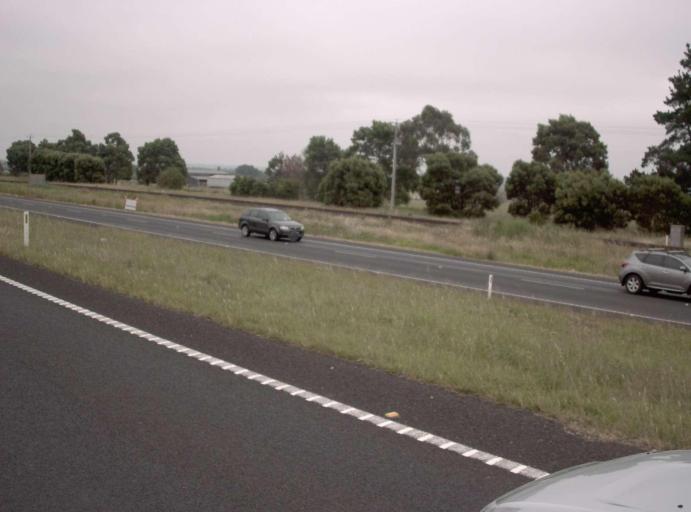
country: AU
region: Victoria
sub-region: Latrobe
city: Moe
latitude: -38.2042
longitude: 146.1787
